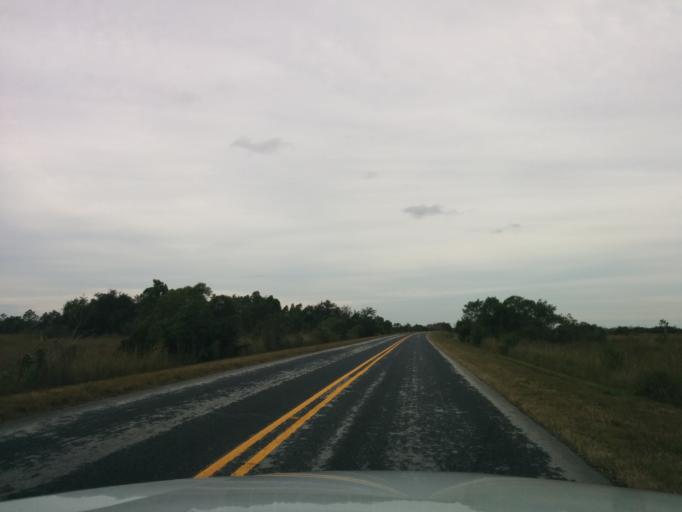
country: US
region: Florida
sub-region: Miami-Dade County
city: Florida City
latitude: 25.4328
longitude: -80.7407
